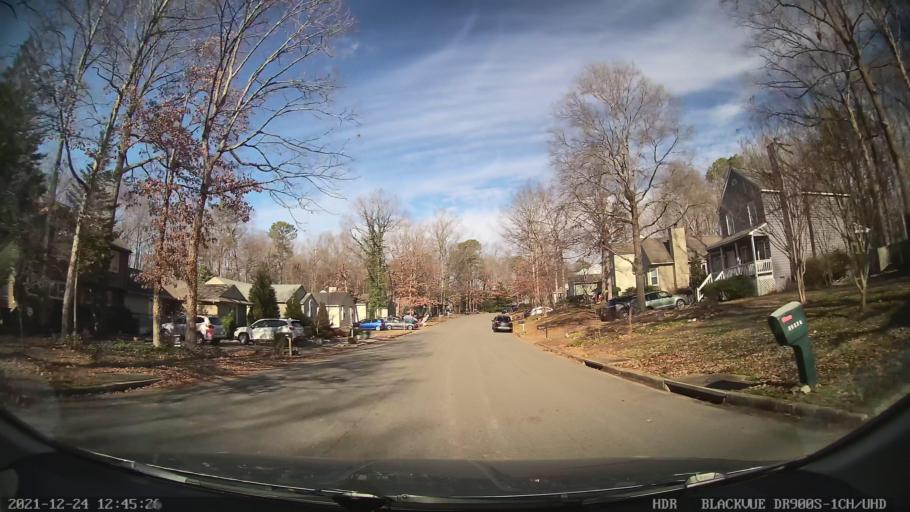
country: US
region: Virginia
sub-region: Henrico County
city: Short Pump
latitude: 37.6312
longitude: -77.6262
